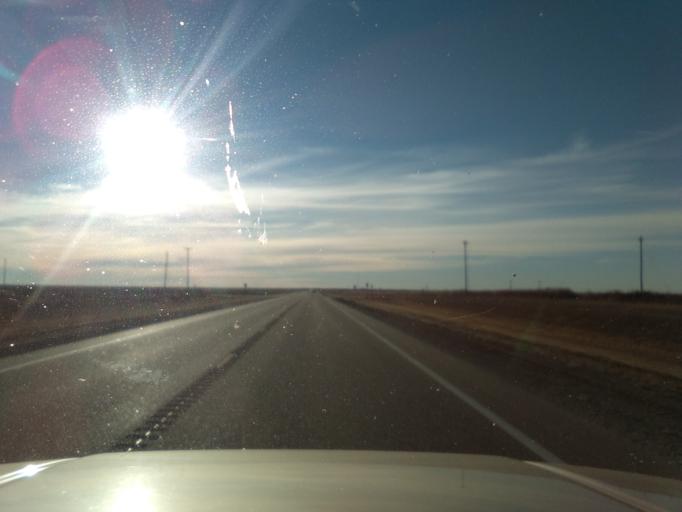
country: US
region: Kansas
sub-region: Sheridan County
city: Hoxie
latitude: 39.4943
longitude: -100.6828
